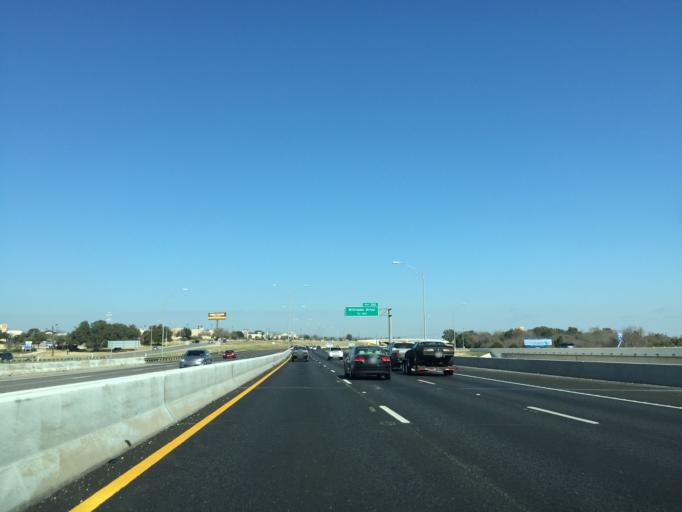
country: US
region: Texas
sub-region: Williamson County
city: Georgetown
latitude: 30.6259
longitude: -97.6910
